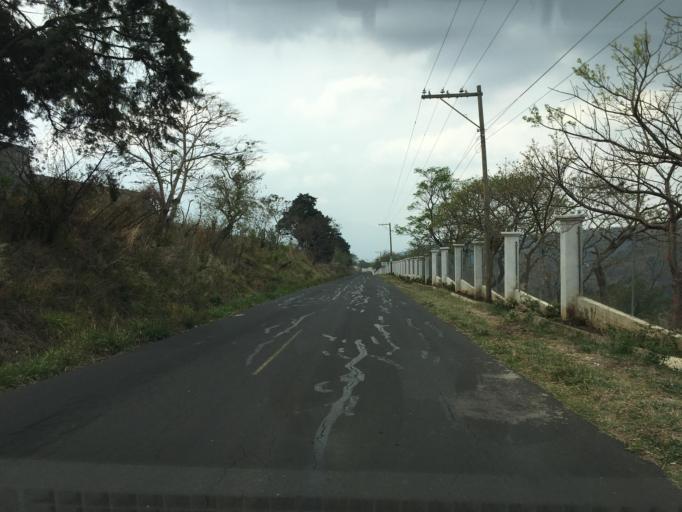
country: GT
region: Escuintla
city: San Vicente Pacaya
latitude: 14.3346
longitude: -90.5654
